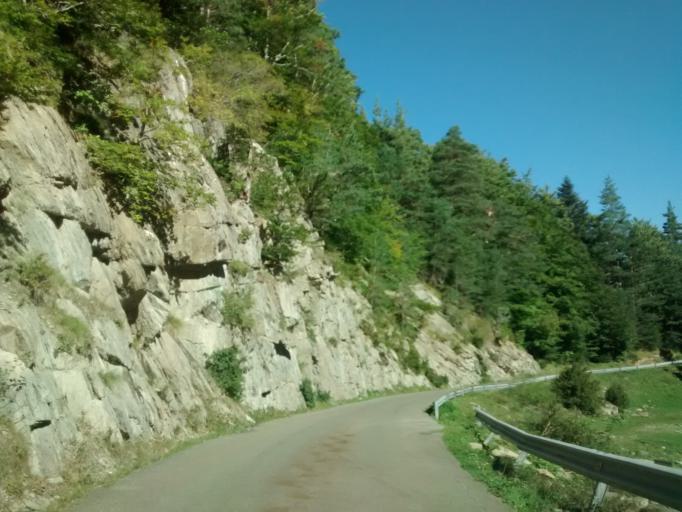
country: ES
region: Aragon
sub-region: Provincia de Huesca
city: Aragues del Puerto
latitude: 42.8192
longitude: -0.7118
